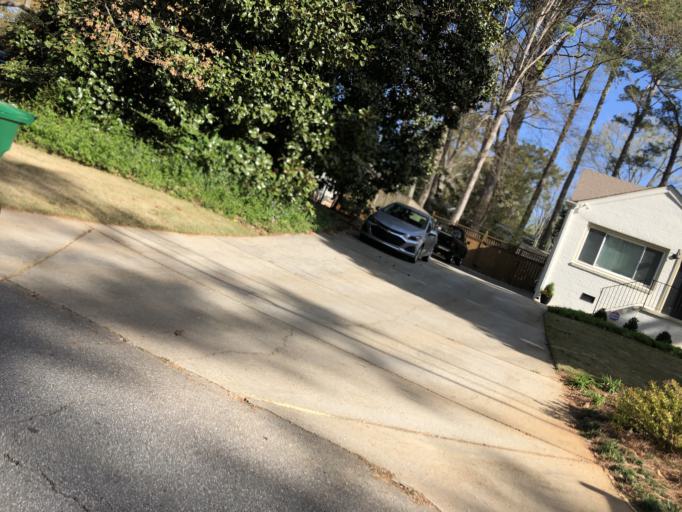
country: US
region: Georgia
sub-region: DeKalb County
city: North Decatur
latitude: 33.8008
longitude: -84.2985
